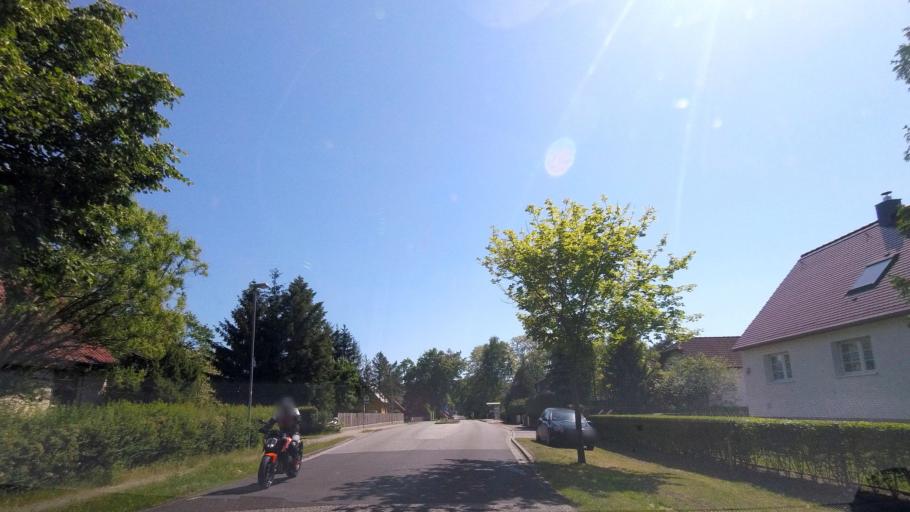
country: DE
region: Brandenburg
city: Gross Kreutz
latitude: 52.3568
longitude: 12.7656
